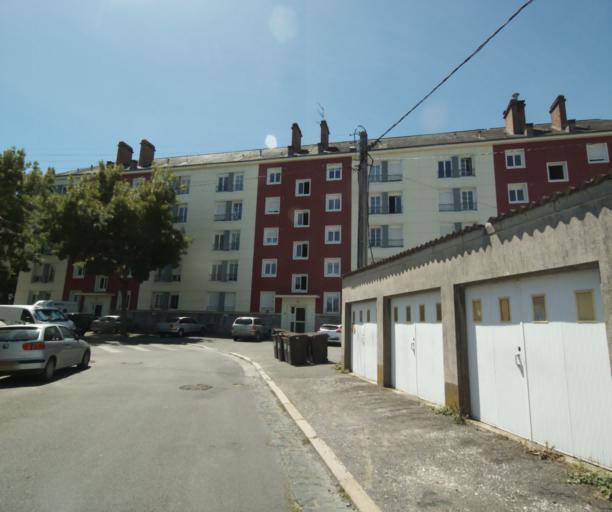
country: FR
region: Pays de la Loire
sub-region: Departement de la Mayenne
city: Laval
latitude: 48.0753
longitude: -0.7578
